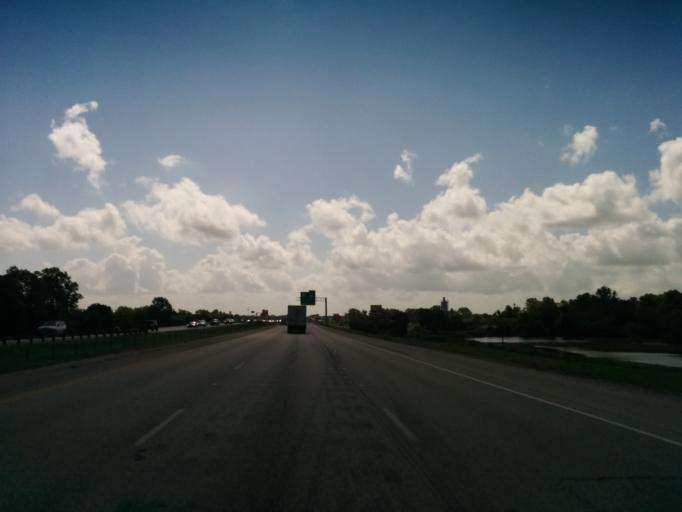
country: US
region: Texas
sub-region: Colorado County
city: Columbus
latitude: 29.6932
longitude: -96.5556
